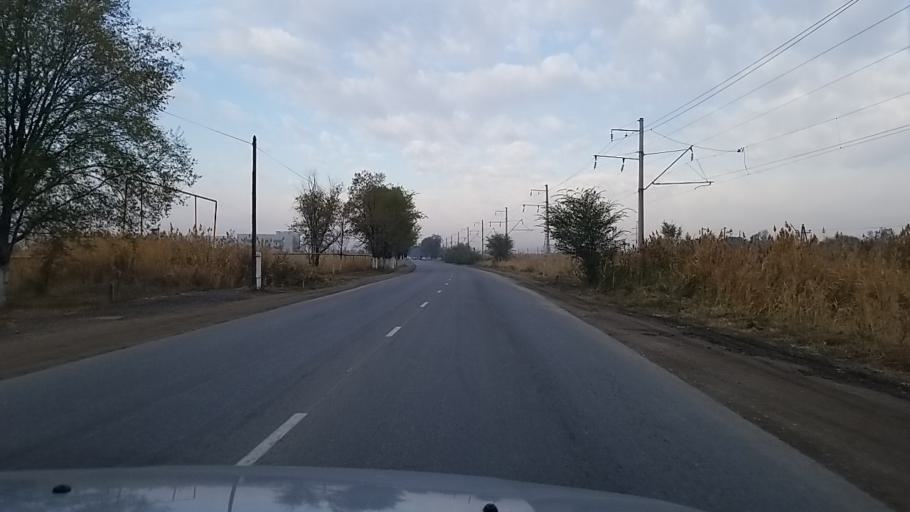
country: KZ
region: Almaty Oblysy
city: Burunday
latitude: 43.3573
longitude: 76.7878
